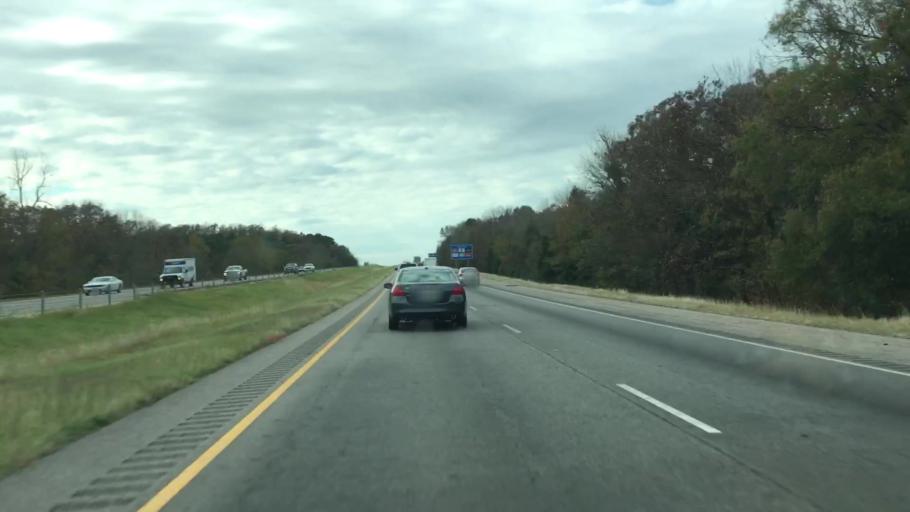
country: US
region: Arkansas
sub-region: Conway County
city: Morrilton
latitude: 35.1681
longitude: -92.6889
